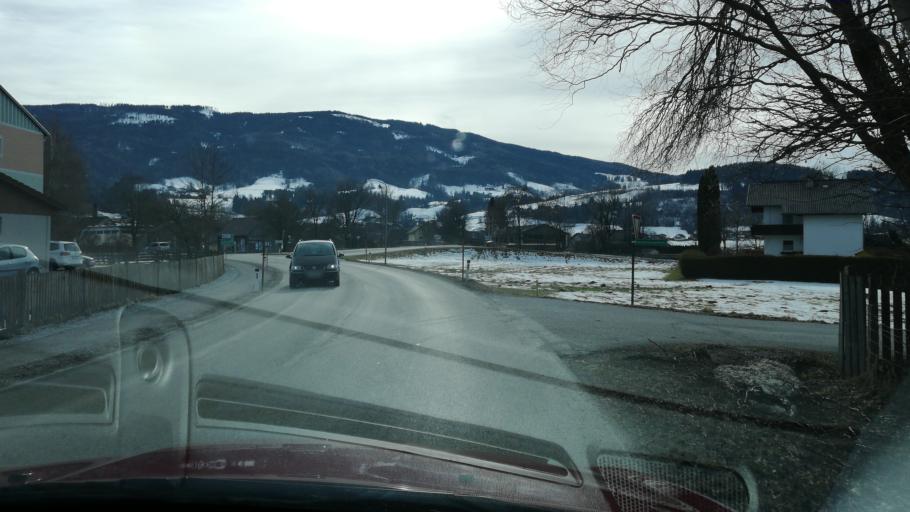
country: AT
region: Styria
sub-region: Politischer Bezirk Liezen
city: Irdning
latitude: 47.5043
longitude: 14.0958
